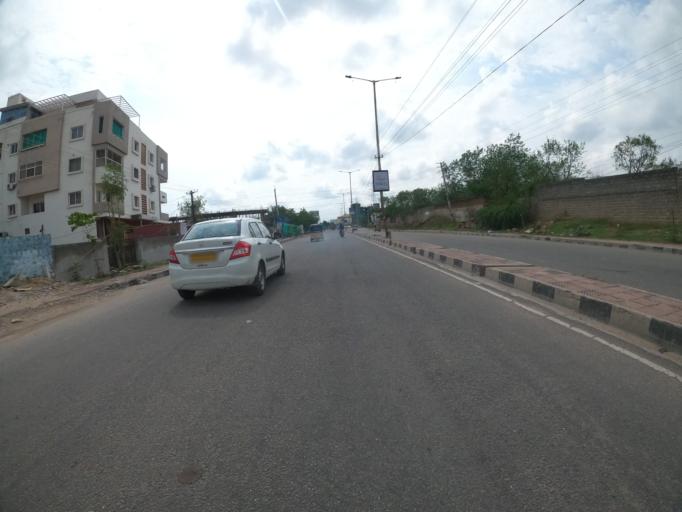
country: IN
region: Telangana
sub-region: Hyderabad
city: Hyderabad
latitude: 17.3814
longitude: 78.3664
